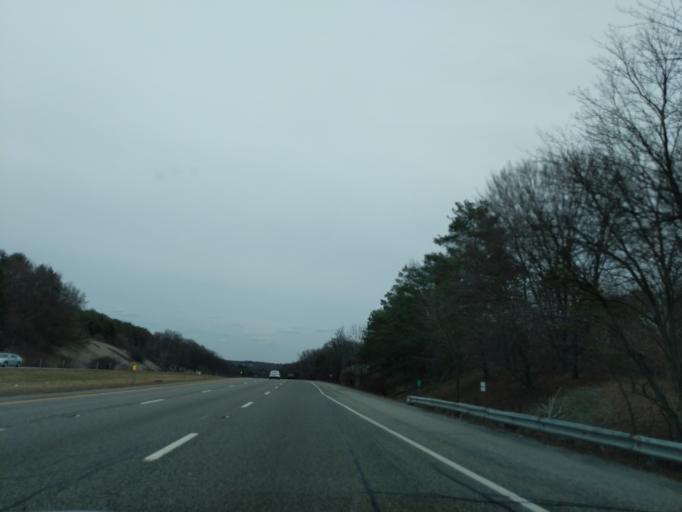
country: US
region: Rhode Island
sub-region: Providence County
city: Cumberland
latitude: 41.9508
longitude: -71.3967
